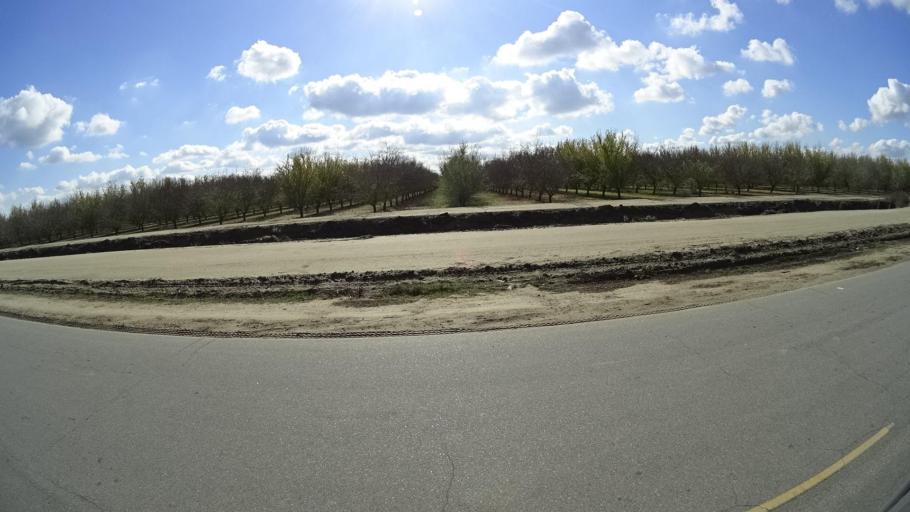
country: US
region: California
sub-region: Kern County
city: McFarland
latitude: 35.6742
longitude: -119.3071
